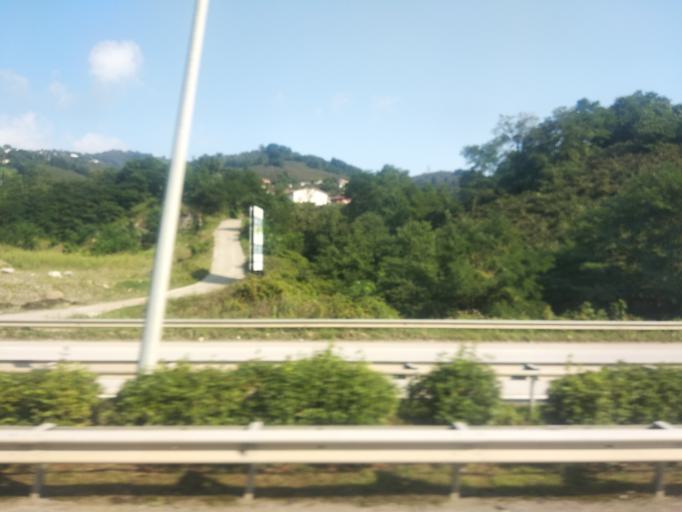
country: TR
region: Ordu
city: Ordu
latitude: 40.9990
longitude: 37.8216
